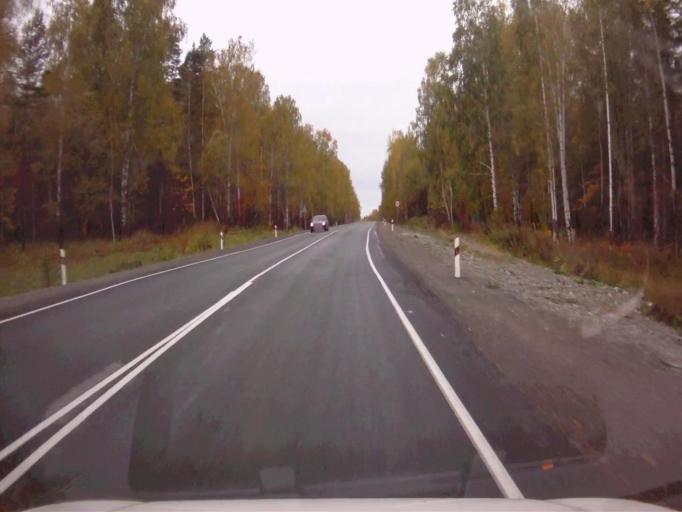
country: RU
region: Chelyabinsk
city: Nyazepetrovsk
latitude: 56.0576
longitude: 59.7343
